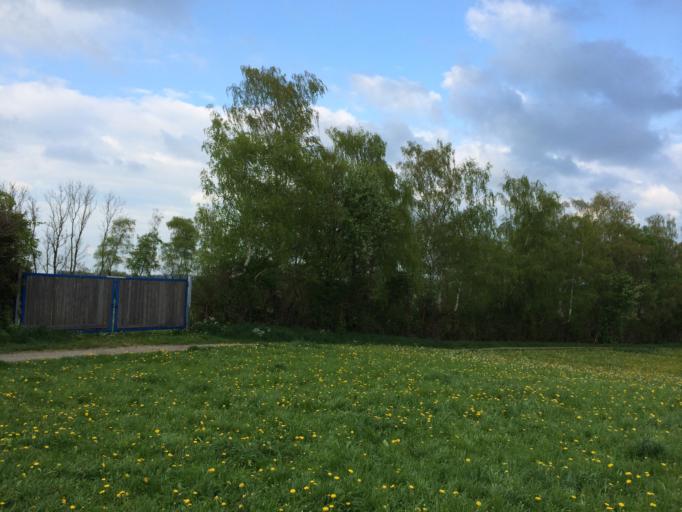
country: DE
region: Bavaria
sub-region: Swabia
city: Kaufbeuren
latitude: 47.8692
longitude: 10.6247
